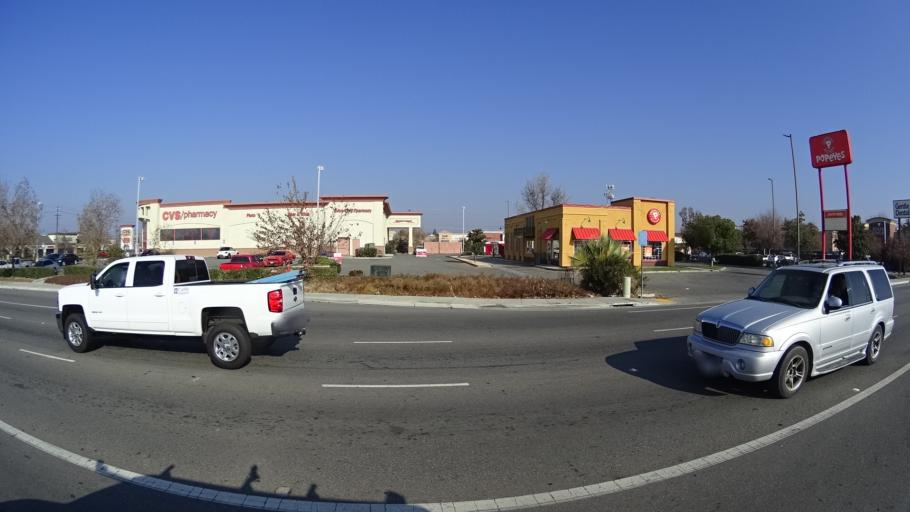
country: US
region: California
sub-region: Kern County
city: Greenacres
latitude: 35.3834
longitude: -119.1090
